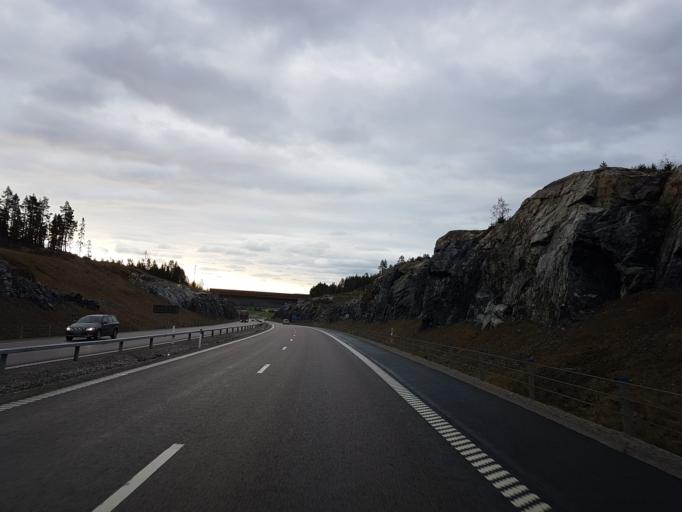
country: SE
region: Vaesternorrland
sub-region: Sundsvalls Kommun
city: Nolby
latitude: 62.3043
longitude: 17.3426
